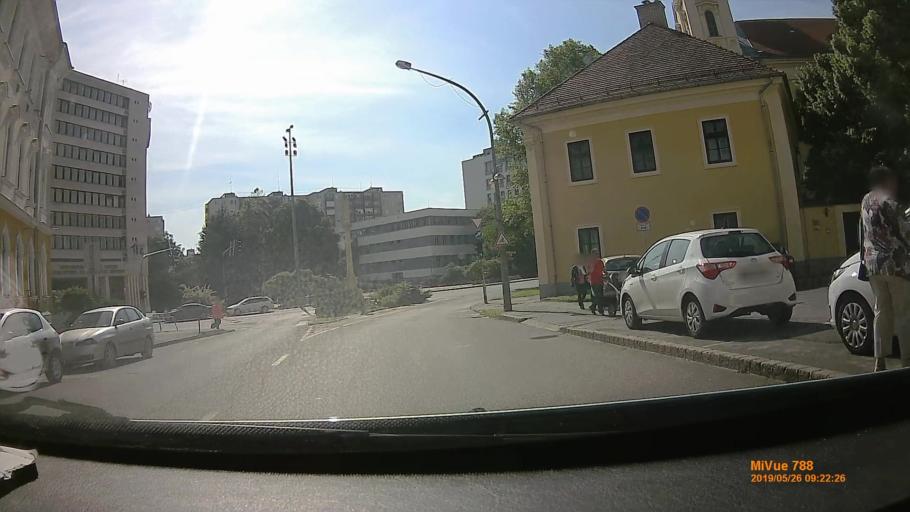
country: HU
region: Borsod-Abauj-Zemplen
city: Miskolc
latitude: 48.0995
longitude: 20.7845
